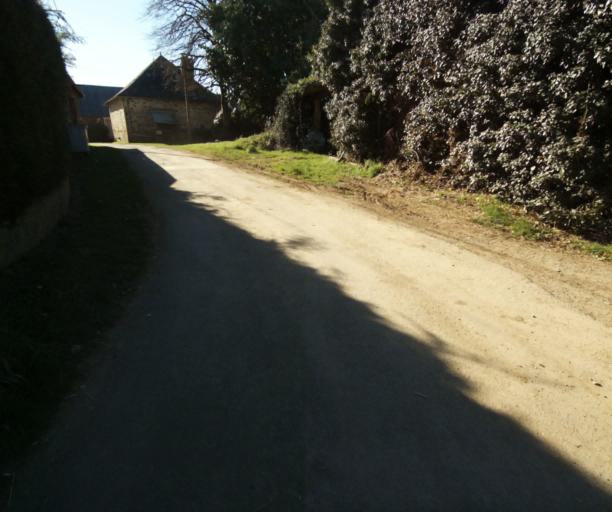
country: FR
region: Limousin
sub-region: Departement de la Correze
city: Seilhac
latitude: 45.3999
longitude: 1.7261
